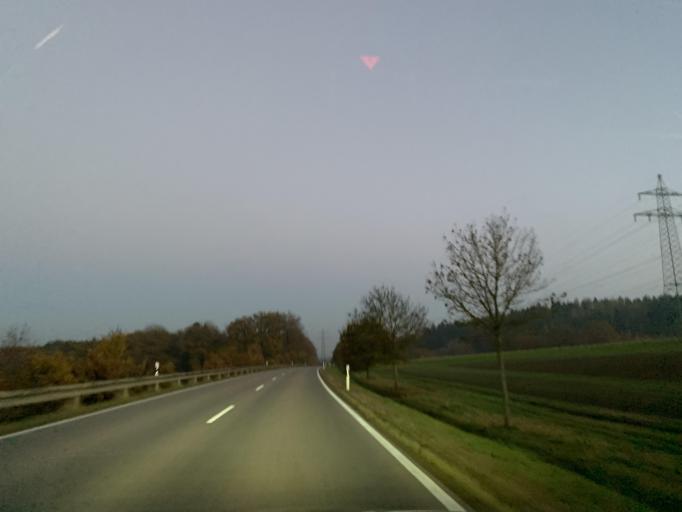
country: DE
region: Bavaria
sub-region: Upper Palatinate
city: Brunn
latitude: 49.2413
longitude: 12.2144
